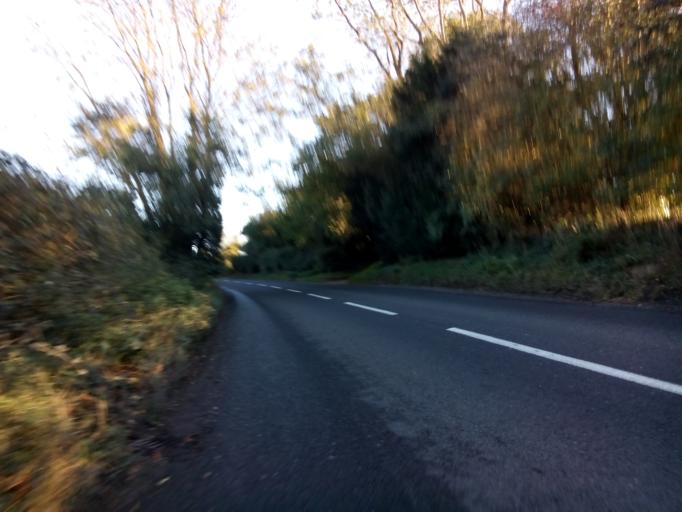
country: GB
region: England
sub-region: Suffolk
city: Sudbury
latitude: 51.9916
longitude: 0.7687
